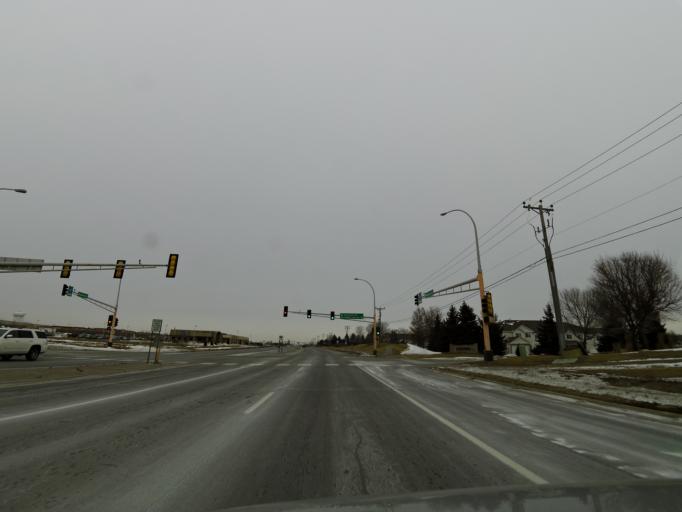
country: US
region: Minnesota
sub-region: Washington County
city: Woodbury
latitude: 44.9376
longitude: -92.9034
